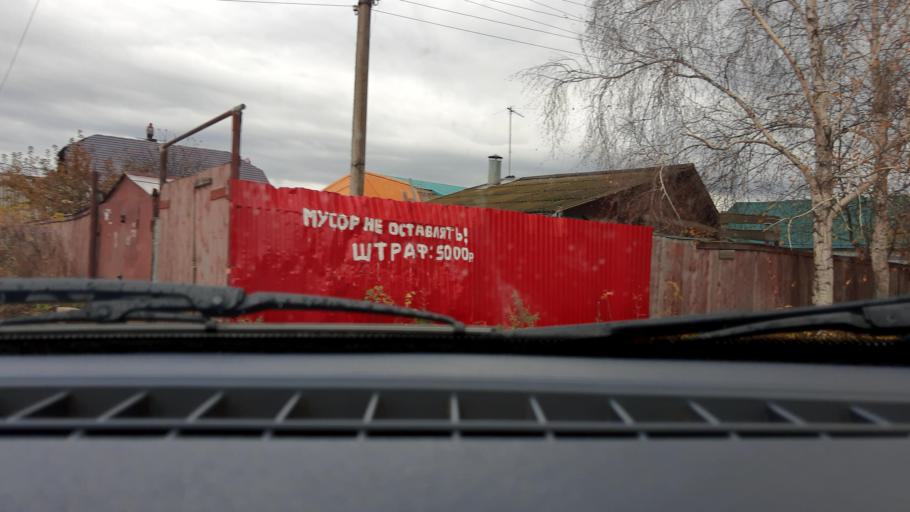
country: RU
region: Bashkortostan
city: Mikhaylovka
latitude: 54.7913
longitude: 55.8845
